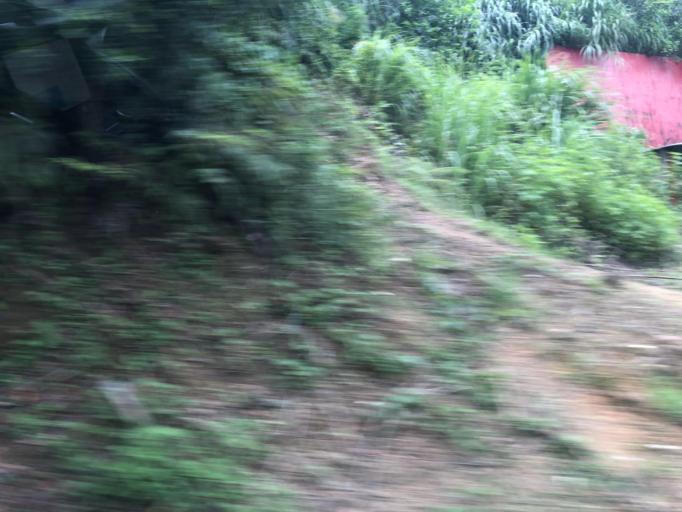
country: TW
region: Taipei
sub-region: Taipei
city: Banqiao
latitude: 24.9183
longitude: 121.4182
